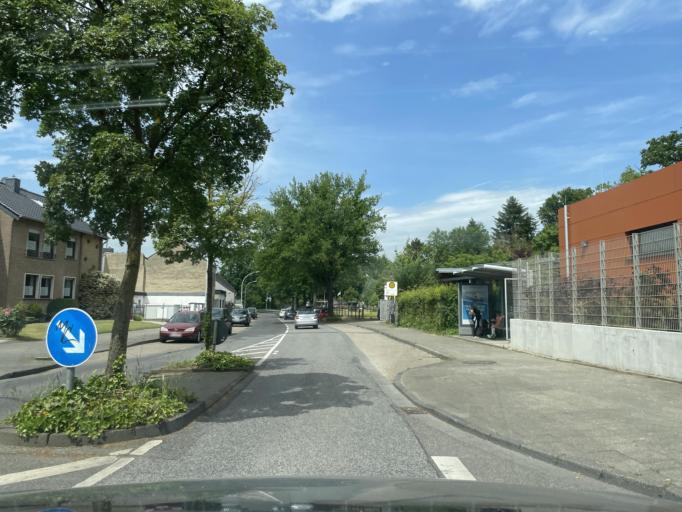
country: DE
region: North Rhine-Westphalia
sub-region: Regierungsbezirk Dusseldorf
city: Monchengladbach
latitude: 51.1265
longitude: 6.4393
